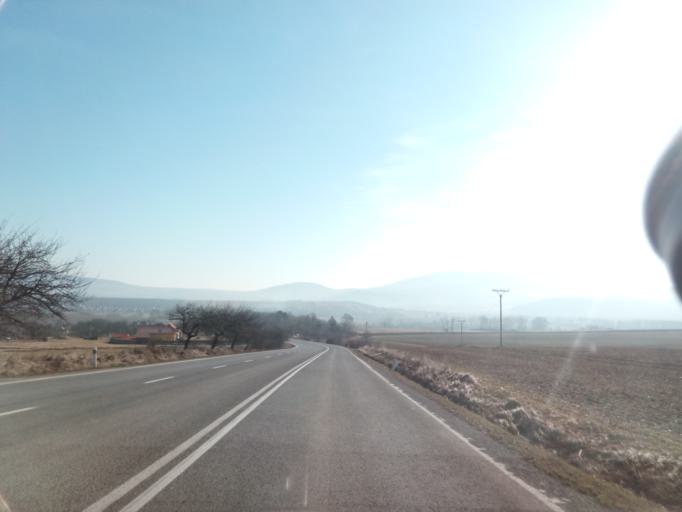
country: SK
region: Kosicky
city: Kosice
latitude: 48.7347
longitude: 21.4078
